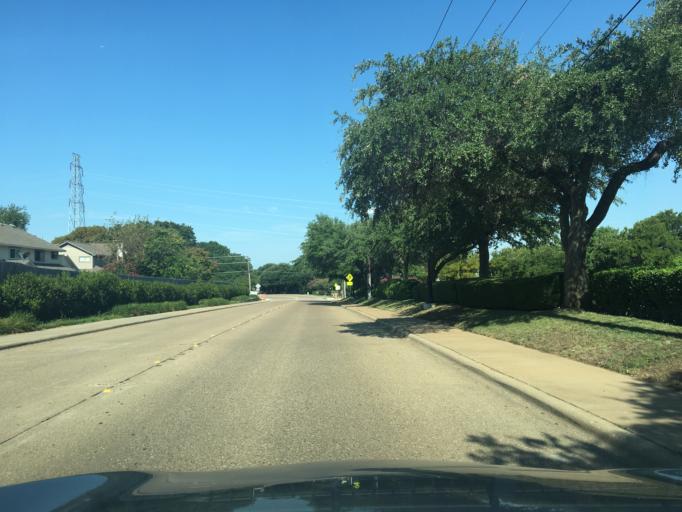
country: US
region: Texas
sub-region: Dallas County
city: Addison
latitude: 32.9513
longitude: -96.8462
